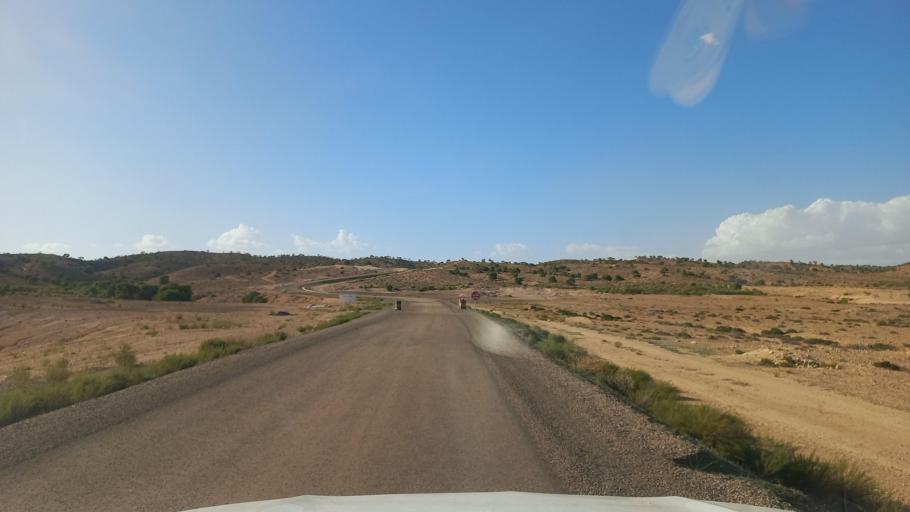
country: TN
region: Al Qasrayn
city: Sbiba
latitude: 35.3540
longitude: 8.9845
